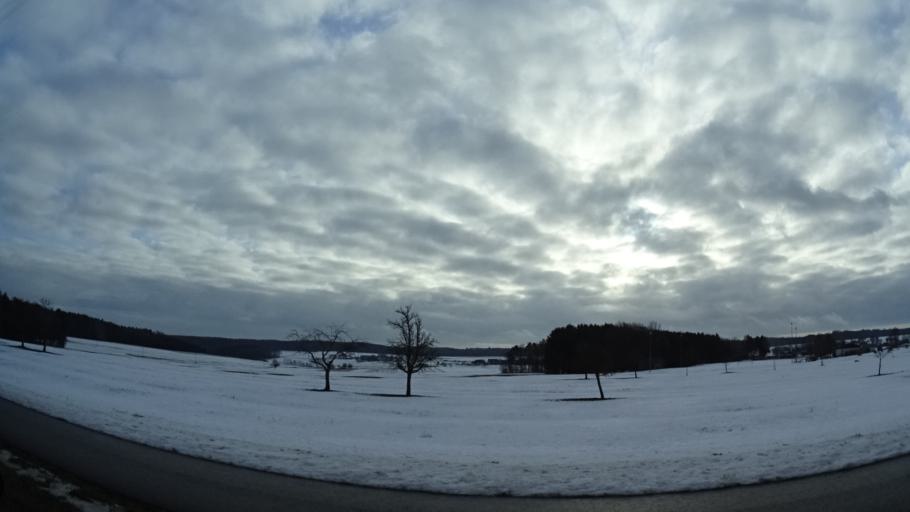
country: DE
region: Baden-Wuerttemberg
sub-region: Karlsruhe Region
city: Mudau
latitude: 49.5098
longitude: 9.1540
